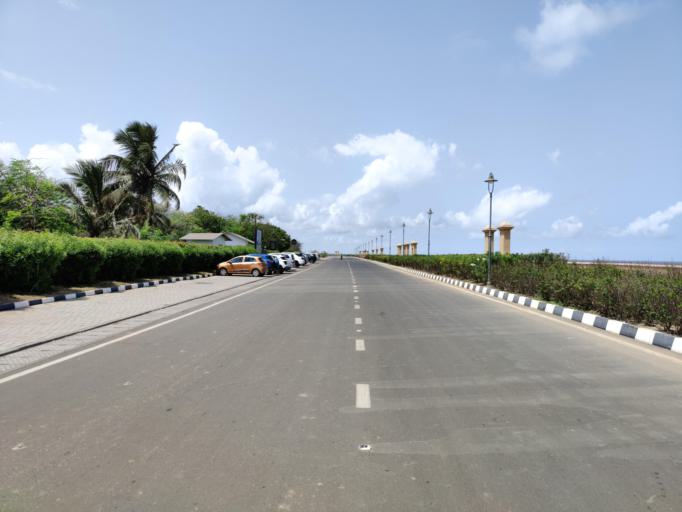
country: IN
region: Daman and Diu
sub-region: Daman District
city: Daman
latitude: 20.4079
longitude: 72.8292
